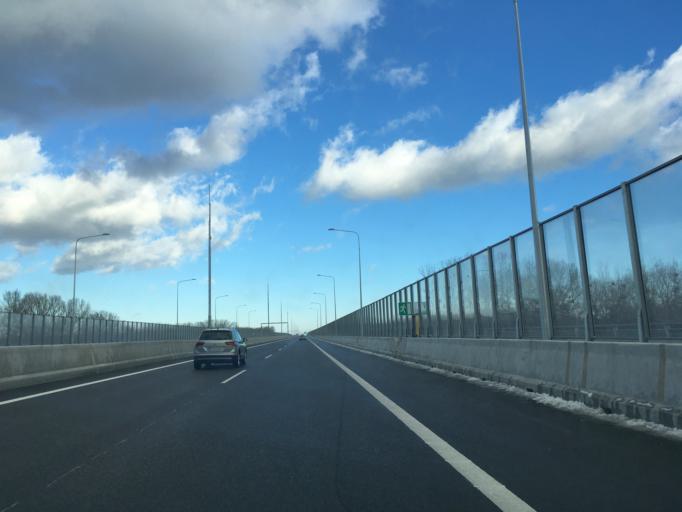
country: AT
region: Burgenland
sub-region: Politischer Bezirk Neusiedl am See
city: Deutsch Jahrndorf
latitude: 48.0792
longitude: 17.1378
